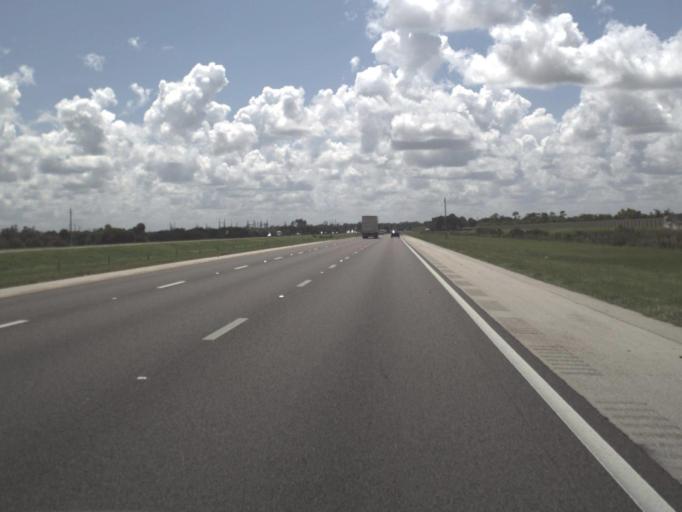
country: US
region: Florida
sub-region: Lee County
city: Bonita Springs
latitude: 26.3644
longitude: -81.7651
